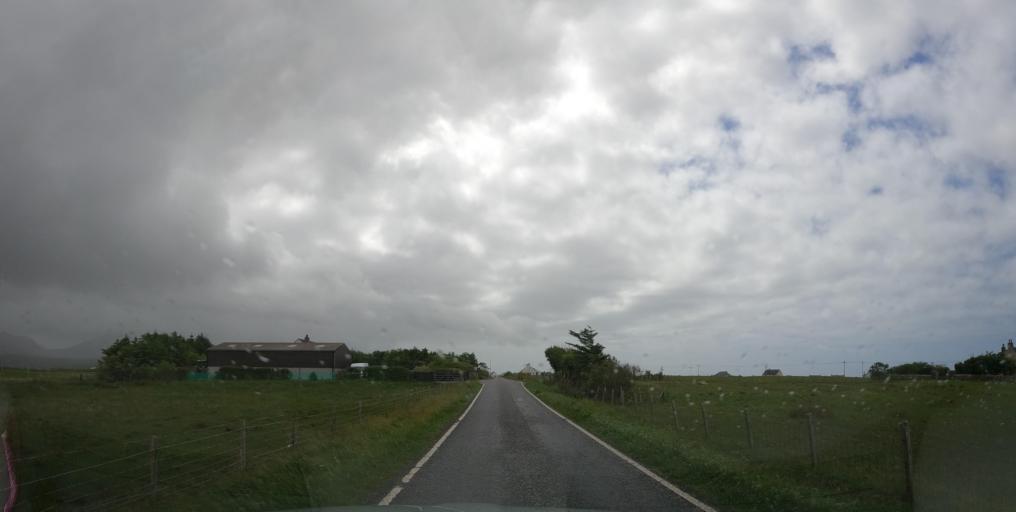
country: GB
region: Scotland
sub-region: Eilean Siar
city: Isle of South Uist
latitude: 57.3258
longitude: -7.3666
